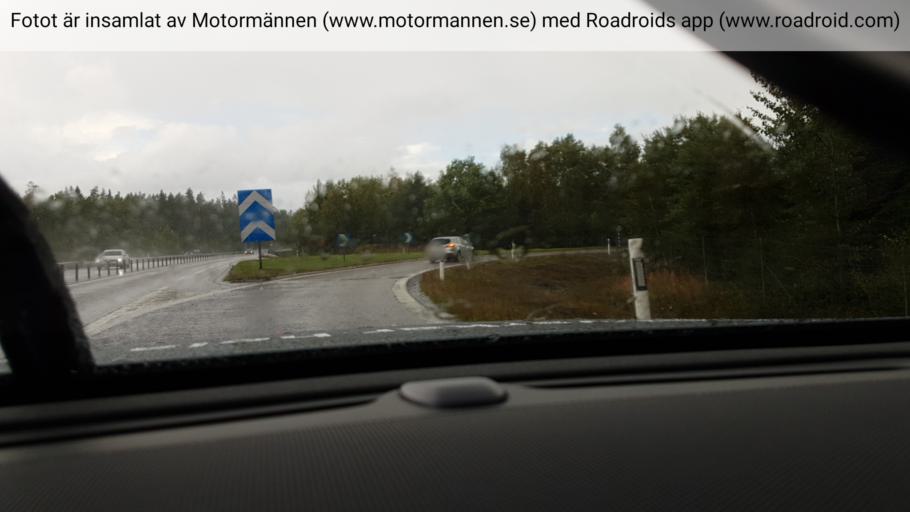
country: SE
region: Vaestra Goetaland
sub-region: Vanersborgs Kommun
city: Vanersborg
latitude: 58.3553
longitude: 12.2583
